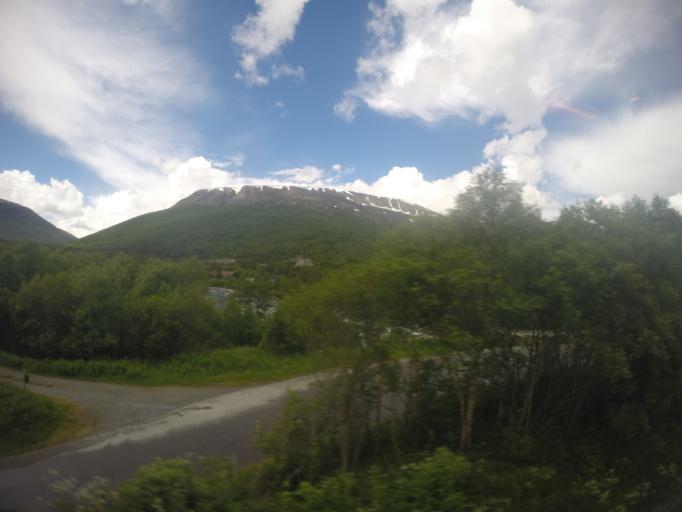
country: NO
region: Sor-Trondelag
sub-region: Oppdal
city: Oppdal
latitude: 62.5074
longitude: 9.5980
